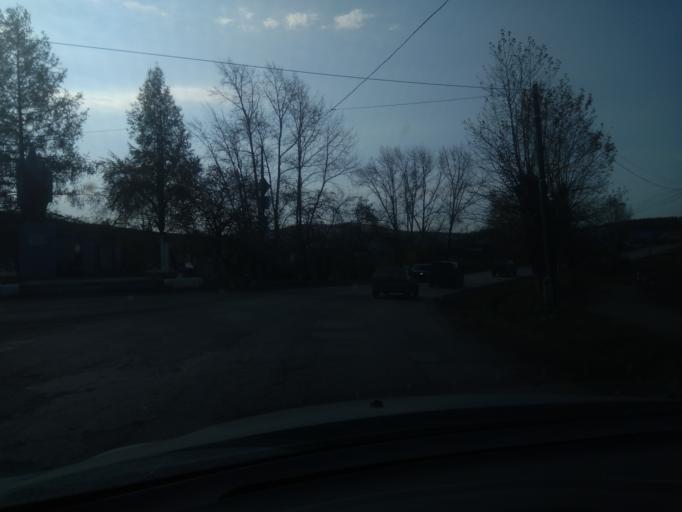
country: RU
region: Sverdlovsk
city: Nizhniye Sergi
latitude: 56.6588
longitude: 59.3013
